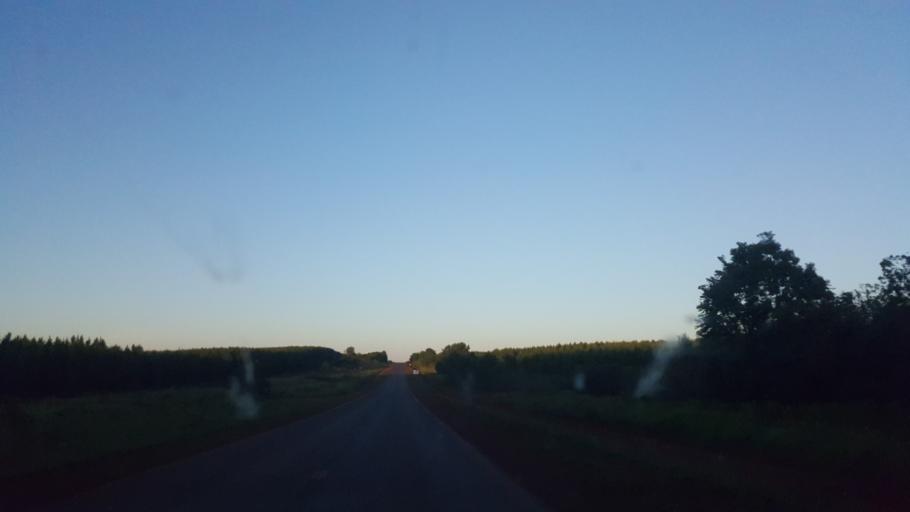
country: AR
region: Corrientes
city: Santo Tome
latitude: -28.4173
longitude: -55.9869
